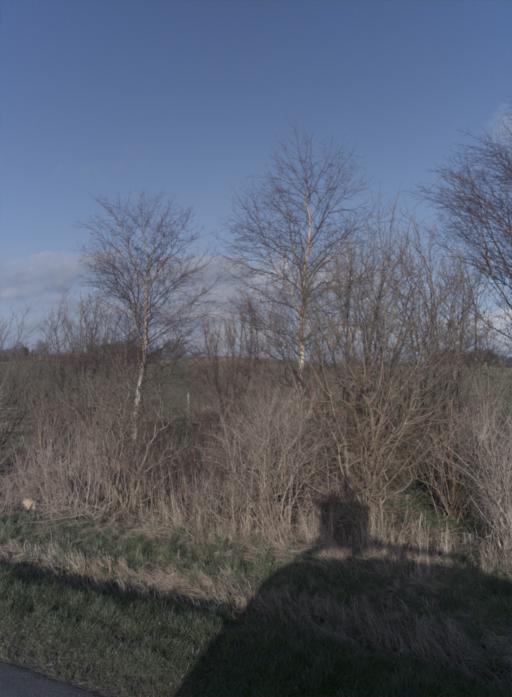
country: DK
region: Zealand
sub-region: Kalundborg Kommune
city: Kalundborg
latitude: 55.6920
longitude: 11.1364
